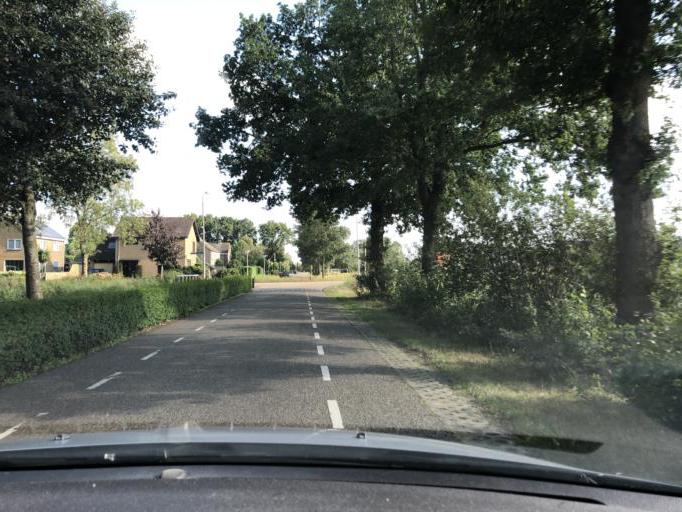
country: NL
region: Overijssel
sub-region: Gemeente Dalfsen
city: Dalfsen
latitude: 52.5847
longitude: 6.2752
